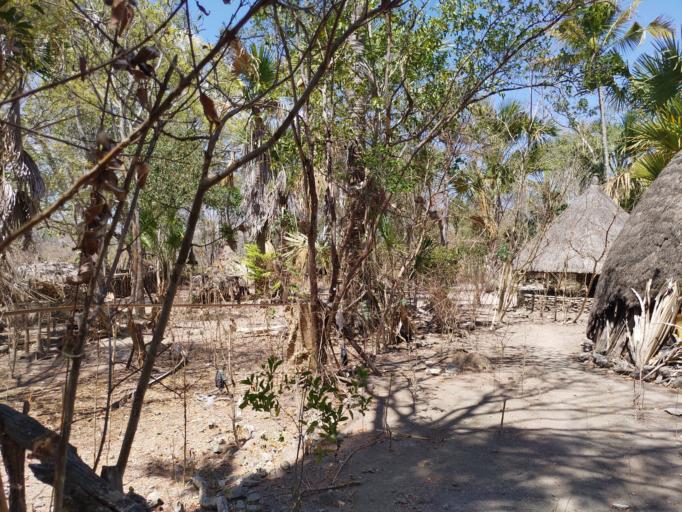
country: ID
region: East Nusa Tenggara
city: Oefau
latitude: -9.9058
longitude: 124.5265
